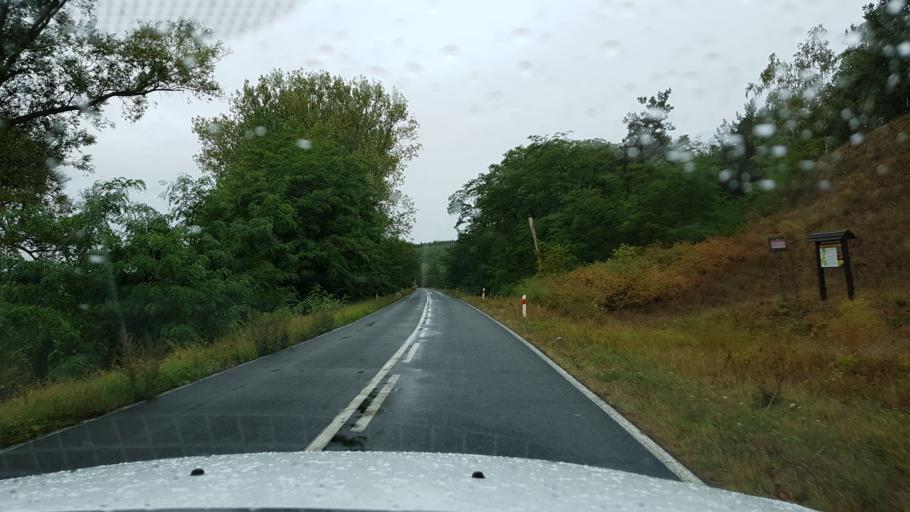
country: PL
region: West Pomeranian Voivodeship
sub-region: Powiat gryfinski
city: Cedynia
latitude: 52.8323
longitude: 14.1694
